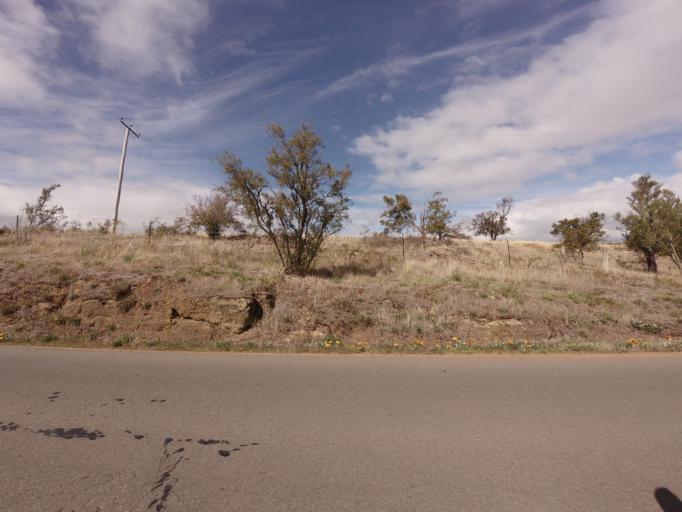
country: AU
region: Tasmania
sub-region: Derwent Valley
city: New Norfolk
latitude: -42.7022
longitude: 146.9166
